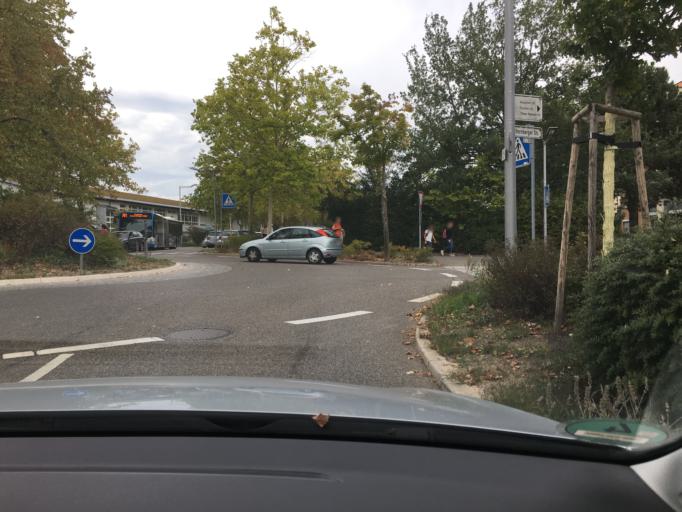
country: DE
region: Baden-Wuerttemberg
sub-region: Regierungsbezirk Stuttgart
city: Boeblingen
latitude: 48.6684
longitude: 9.0053
